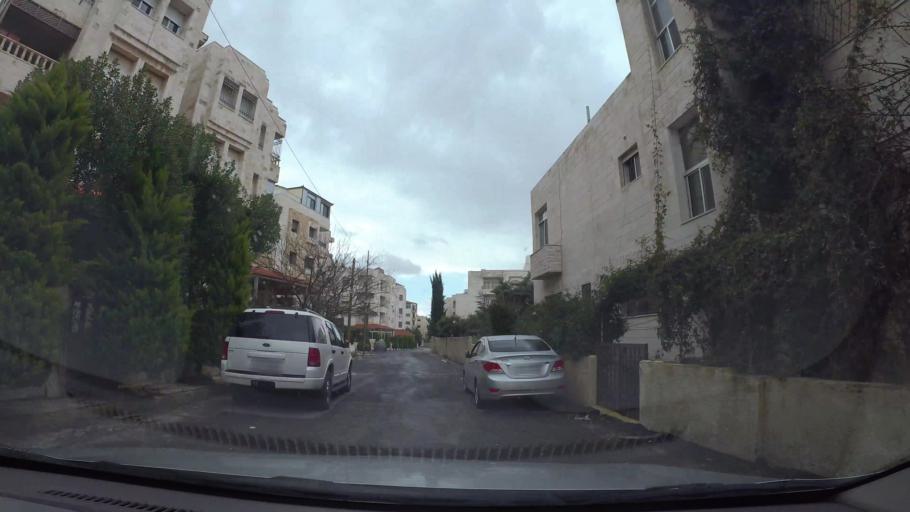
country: JO
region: Amman
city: Al Jubayhah
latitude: 31.9884
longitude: 35.8623
